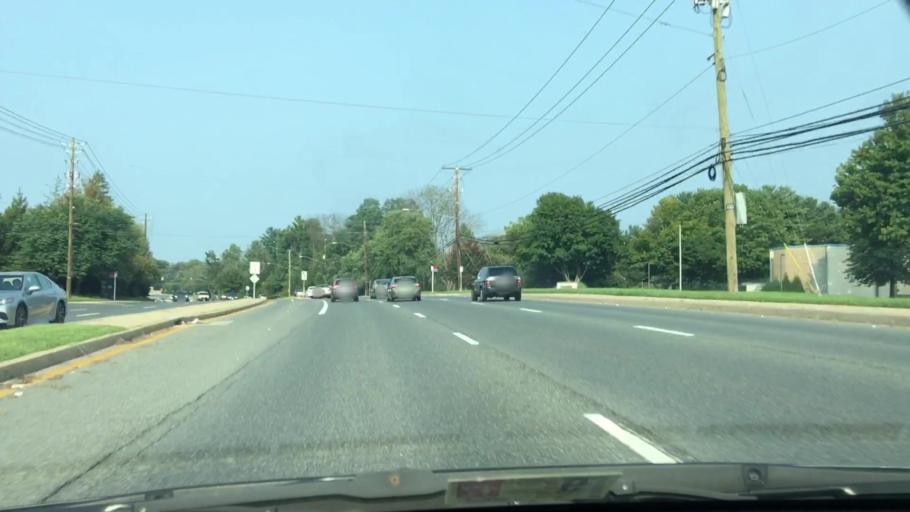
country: US
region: Maryland
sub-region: Montgomery County
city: Colesville
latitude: 39.0663
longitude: -77.0205
